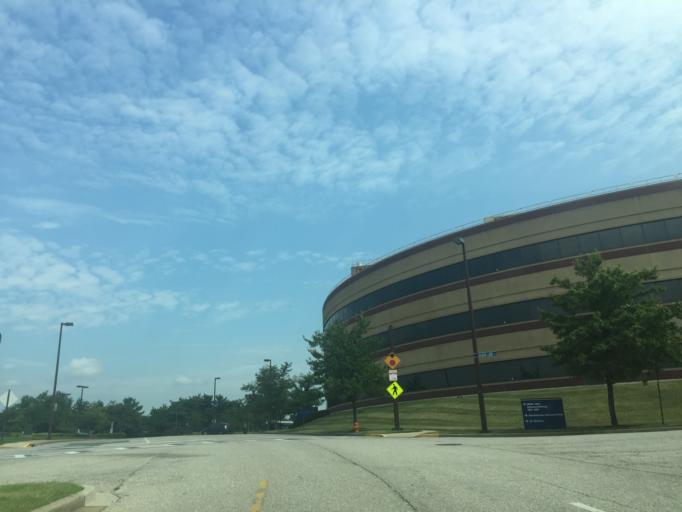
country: US
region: Maryland
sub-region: Baltimore County
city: Dundalk
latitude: 39.2878
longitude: -76.5521
